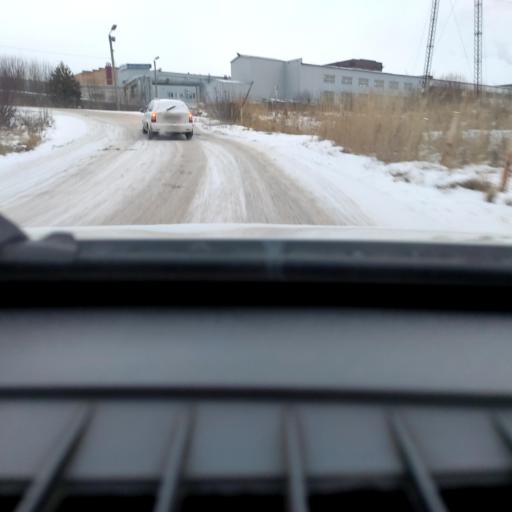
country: RU
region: Perm
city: Perm
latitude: 58.1066
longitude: 56.3689
